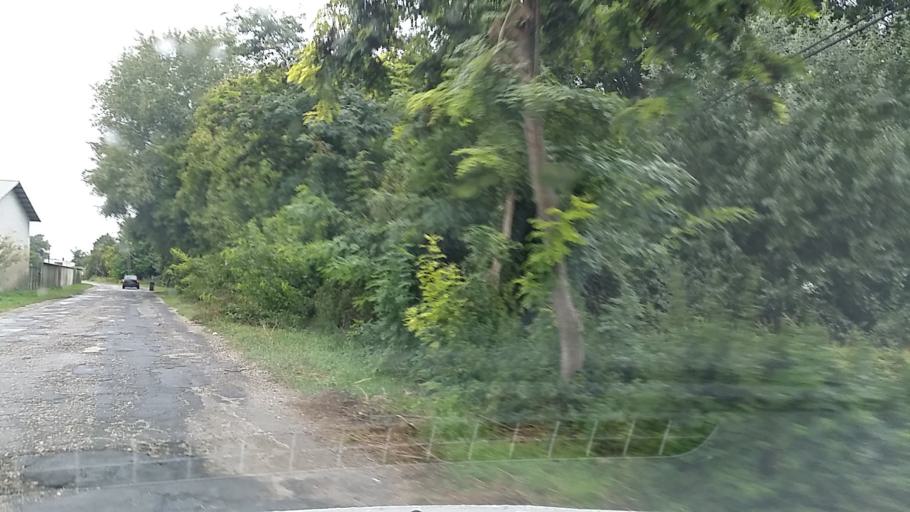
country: HU
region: Pest
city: Domsod
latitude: 47.0780
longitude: 18.9823
